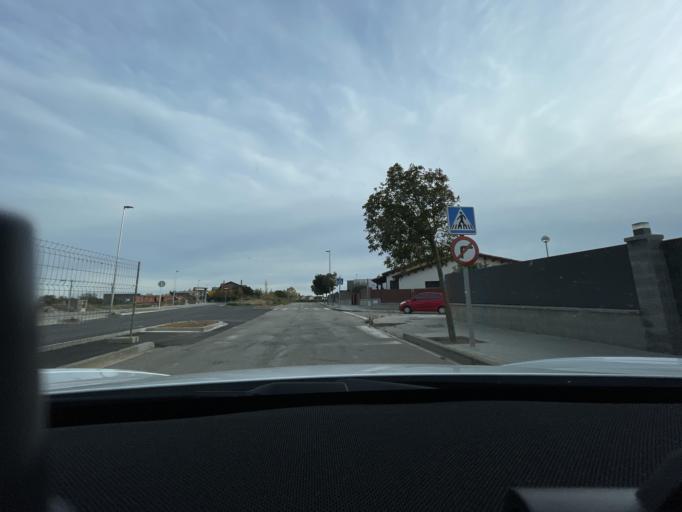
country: ES
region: Catalonia
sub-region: Provincia de Lleida
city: Solsona
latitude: 41.9961
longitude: 1.5287
